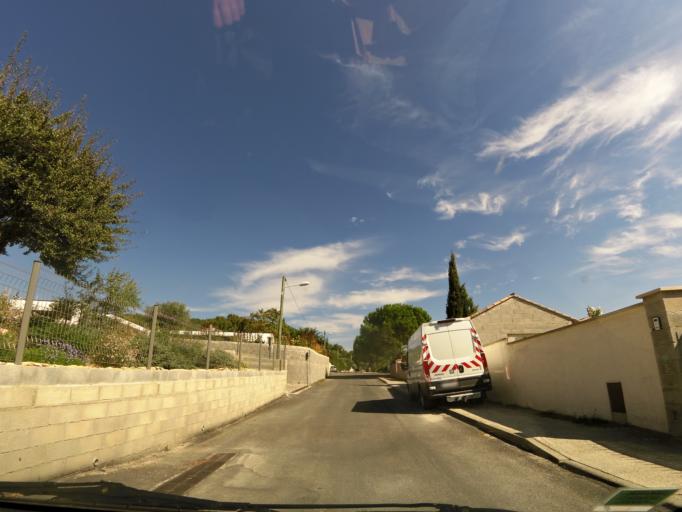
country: FR
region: Languedoc-Roussillon
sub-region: Departement du Gard
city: Nages-et-Solorgues
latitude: 43.7878
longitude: 4.2352
